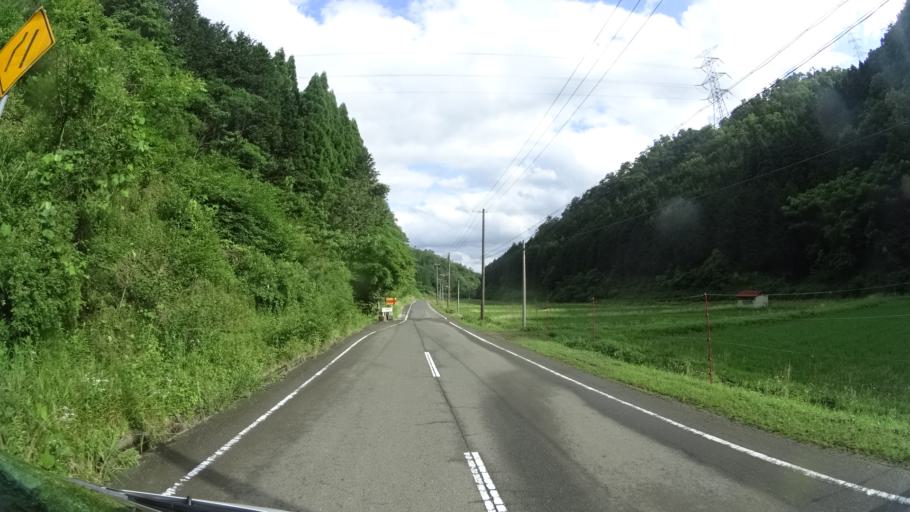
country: JP
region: Kyoto
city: Ayabe
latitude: 35.3702
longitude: 135.2879
